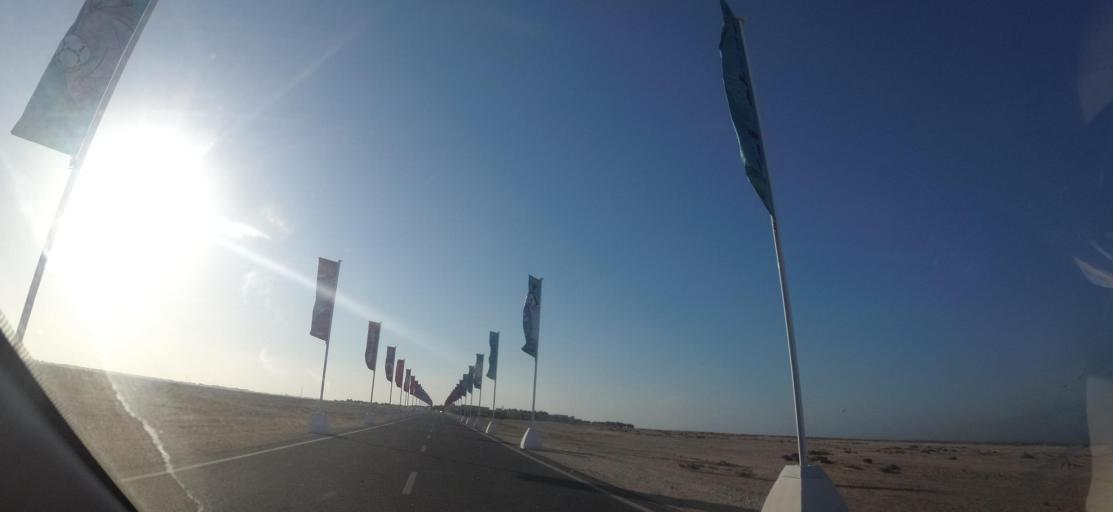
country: QA
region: Madinat ash Shamal
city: Ar Ru'ays
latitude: 26.1550
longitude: 51.2496
